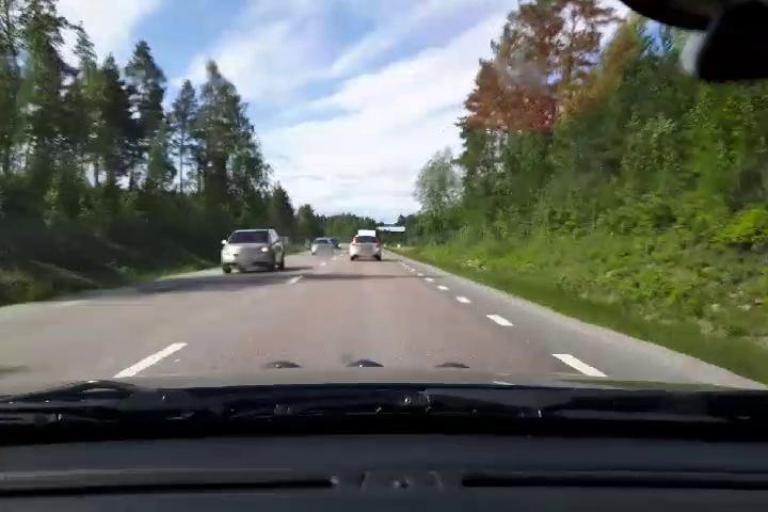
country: SE
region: Gaevleborg
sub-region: Bollnas Kommun
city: Kilafors
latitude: 61.2811
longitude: 16.5205
